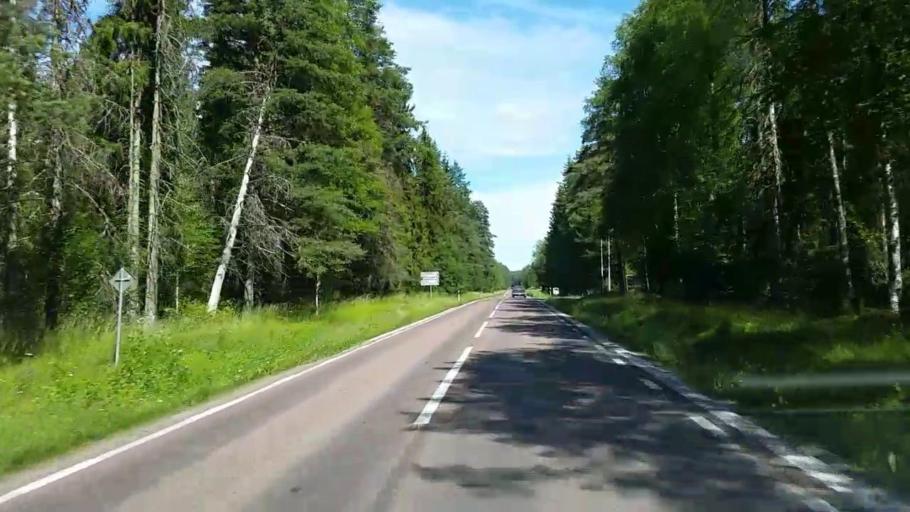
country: SE
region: Dalarna
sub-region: Rattviks Kommun
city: Raettvik
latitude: 60.9020
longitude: 15.1864
